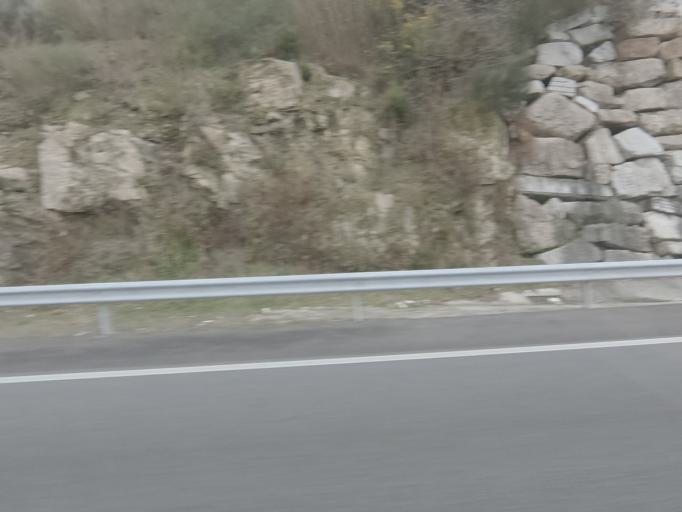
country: ES
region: Galicia
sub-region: Provincia de Ourense
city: Punxin
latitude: 42.3757
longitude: -7.9921
